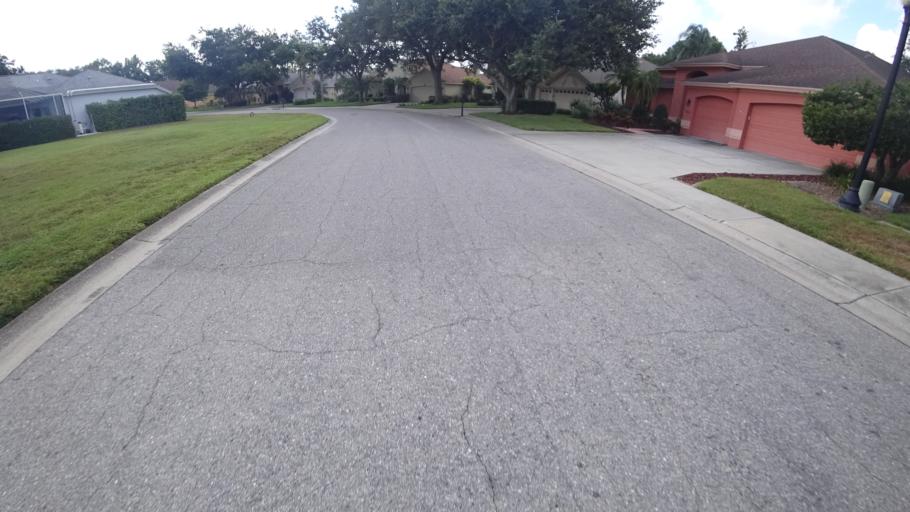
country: US
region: Florida
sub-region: Sarasota County
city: The Meadows
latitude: 27.4302
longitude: -82.4378
